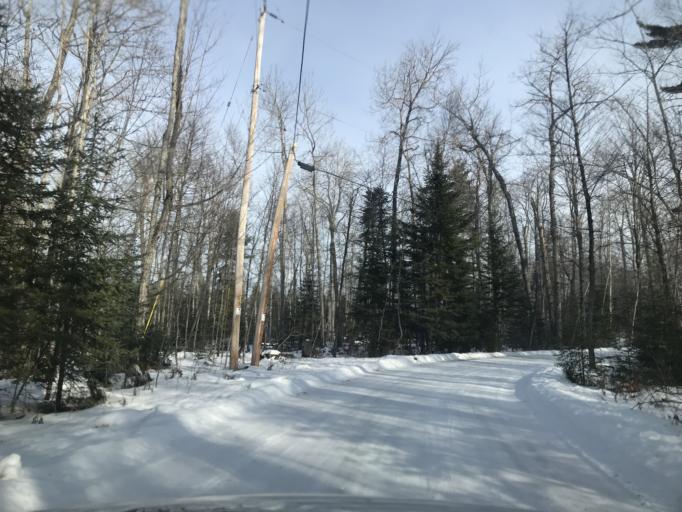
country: US
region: Wisconsin
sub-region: Door County
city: Sturgeon Bay
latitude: 45.1544
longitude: -87.0518
